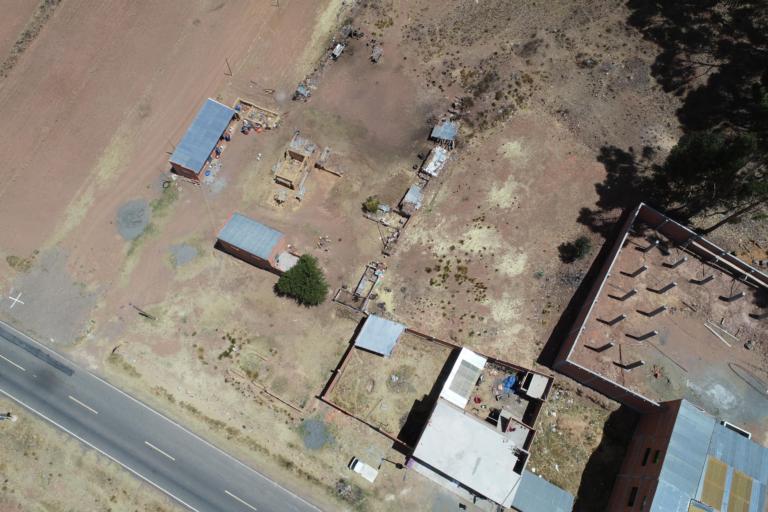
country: BO
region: La Paz
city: Achacachi
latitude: -15.9108
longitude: -68.8866
